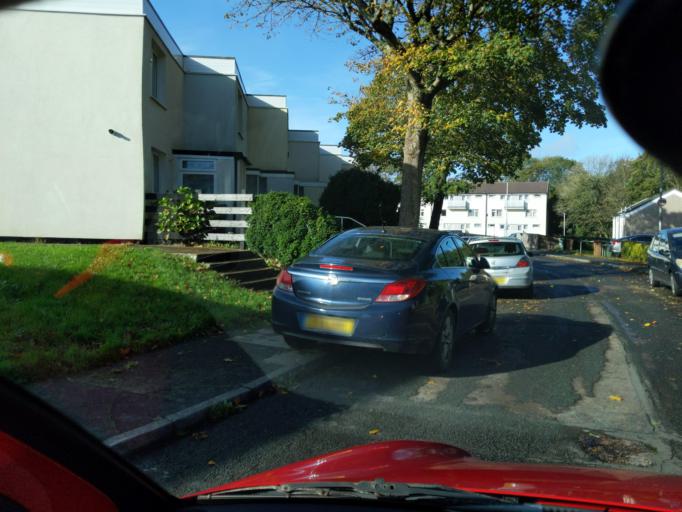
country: GB
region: England
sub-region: Plymouth
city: Plymouth
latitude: 50.4150
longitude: -4.1595
